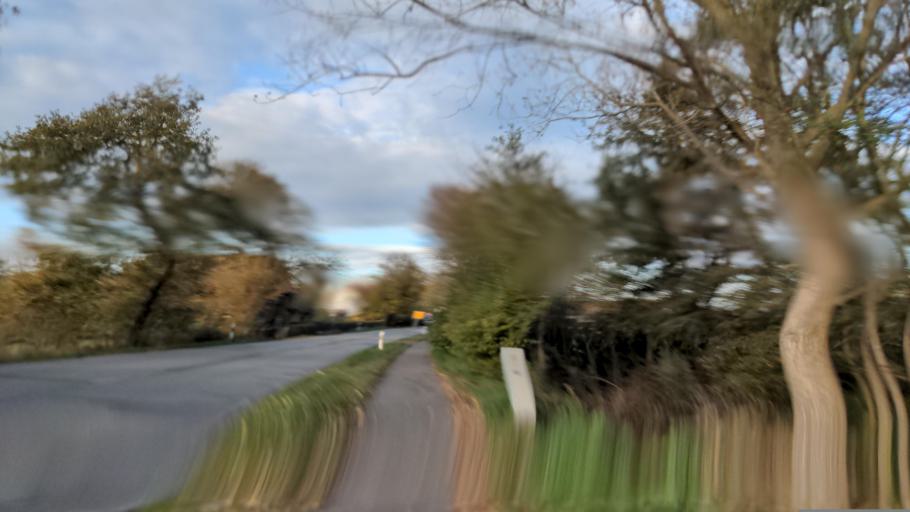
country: DE
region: Schleswig-Holstein
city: Heidekamp
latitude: 53.8459
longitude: 10.5000
